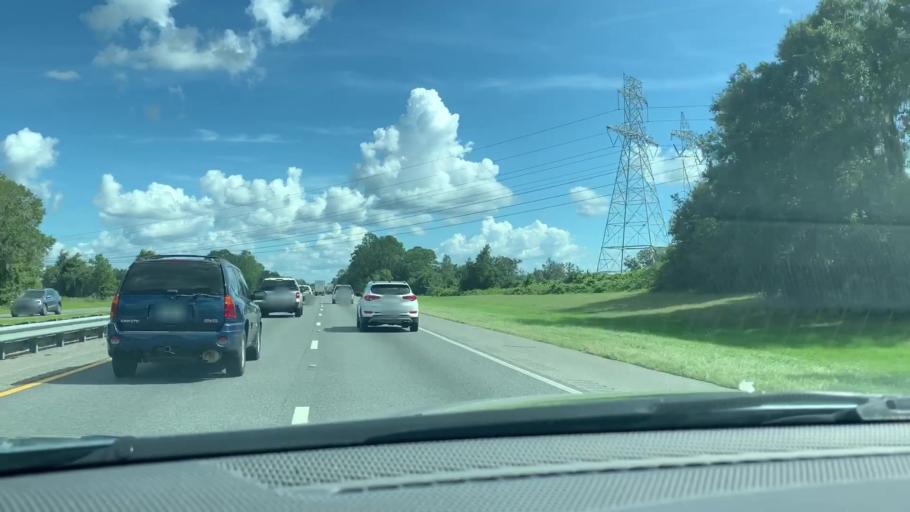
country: US
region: Florida
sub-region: Sumter County
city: Wildwood
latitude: 28.8143
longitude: -82.0154
